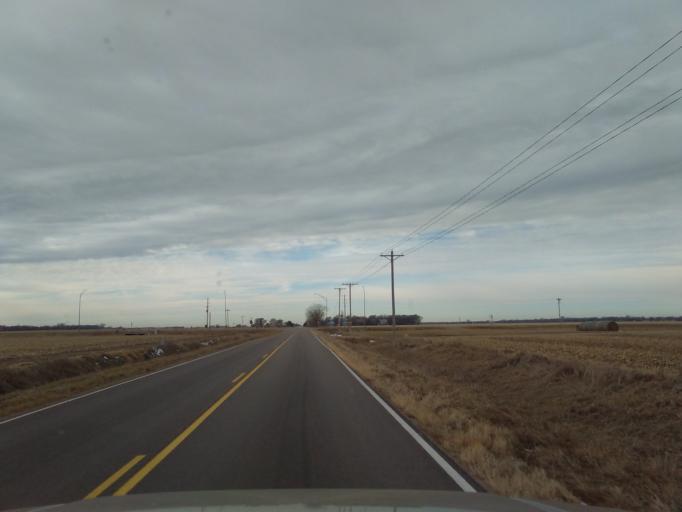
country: US
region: Nebraska
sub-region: Kearney County
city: Minden
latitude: 40.6411
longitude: -98.9491
